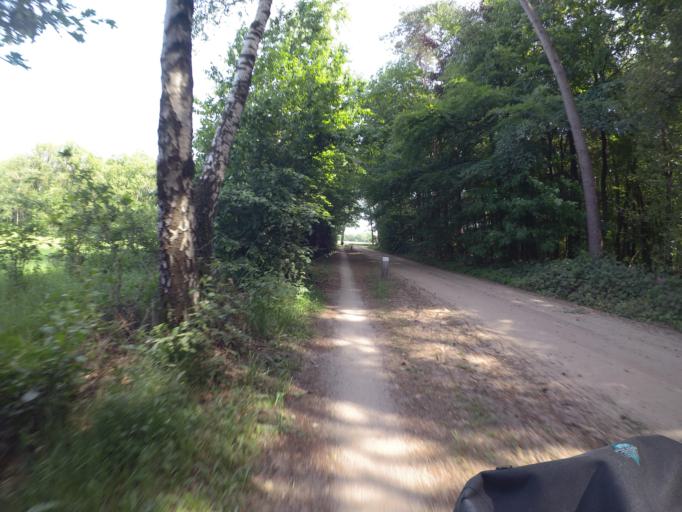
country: NL
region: Gelderland
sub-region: Gemeente Winterswijk
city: Winterswijk
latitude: 51.9356
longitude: 6.6852
